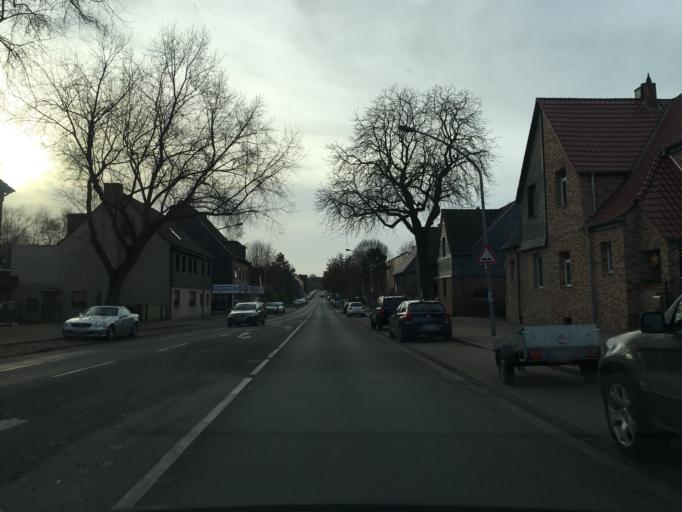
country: DE
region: North Rhine-Westphalia
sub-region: Regierungsbezirk Dusseldorf
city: Dinslaken
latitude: 51.5333
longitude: 6.8081
